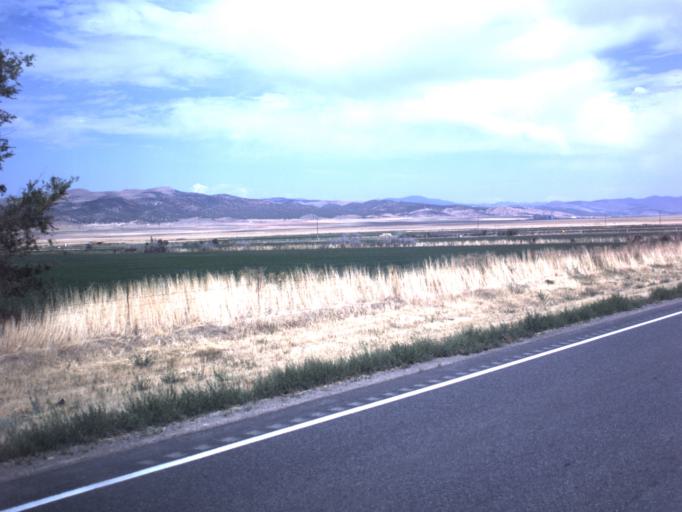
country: US
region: Utah
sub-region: Juab County
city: Nephi
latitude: 39.5670
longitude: -111.8619
